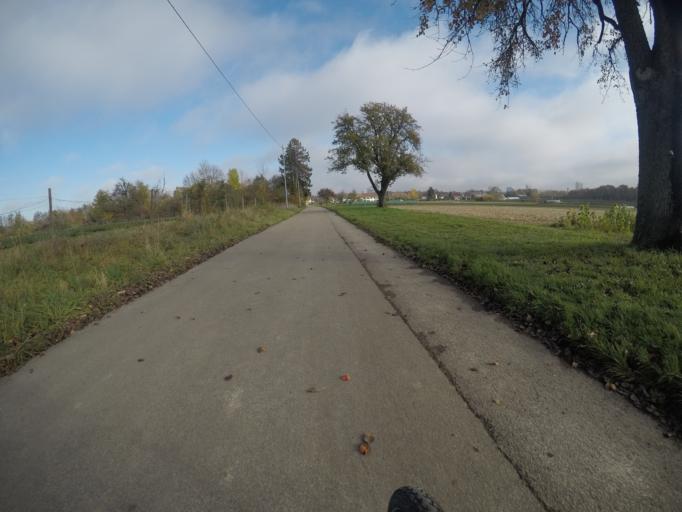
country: DE
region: Baden-Wuerttemberg
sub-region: Regierungsbezirk Stuttgart
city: Leinfelden-Echterdingen
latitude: 48.7218
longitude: 9.1372
